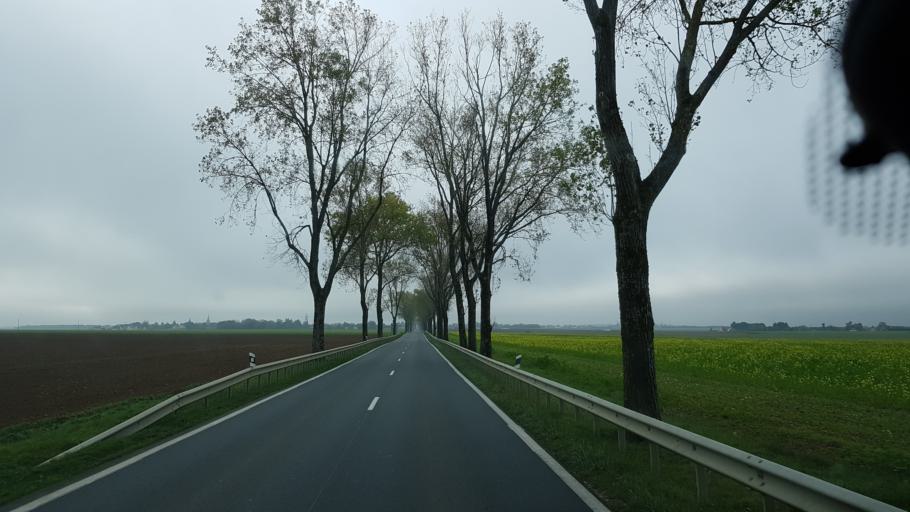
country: FR
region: Ile-de-France
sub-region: Departement de l'Essonne
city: Corbreuse
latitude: 48.4423
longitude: 1.9577
